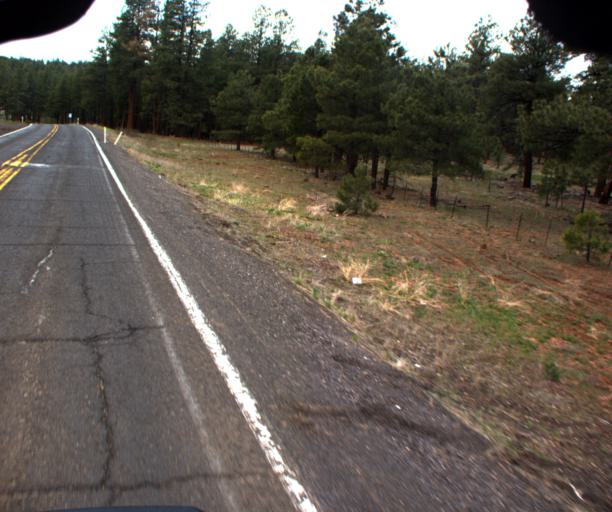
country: US
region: Arizona
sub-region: Coconino County
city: Kachina Village
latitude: 35.1214
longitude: -111.7046
